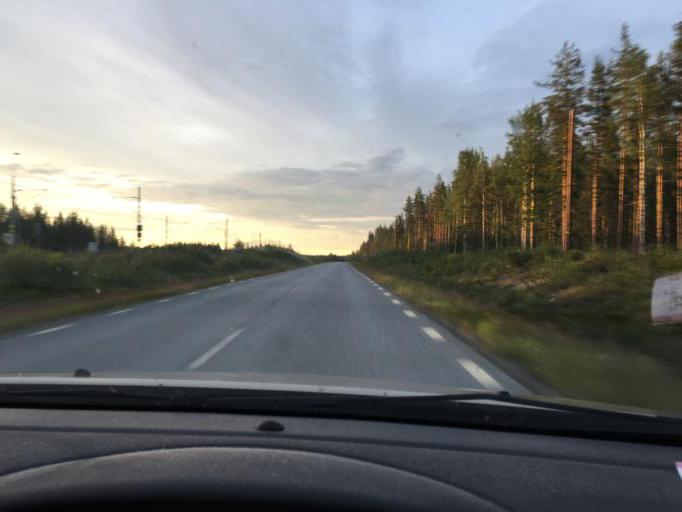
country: SE
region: Norrbotten
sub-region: Lulea Kommun
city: Ranea
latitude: 66.0436
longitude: 22.3419
